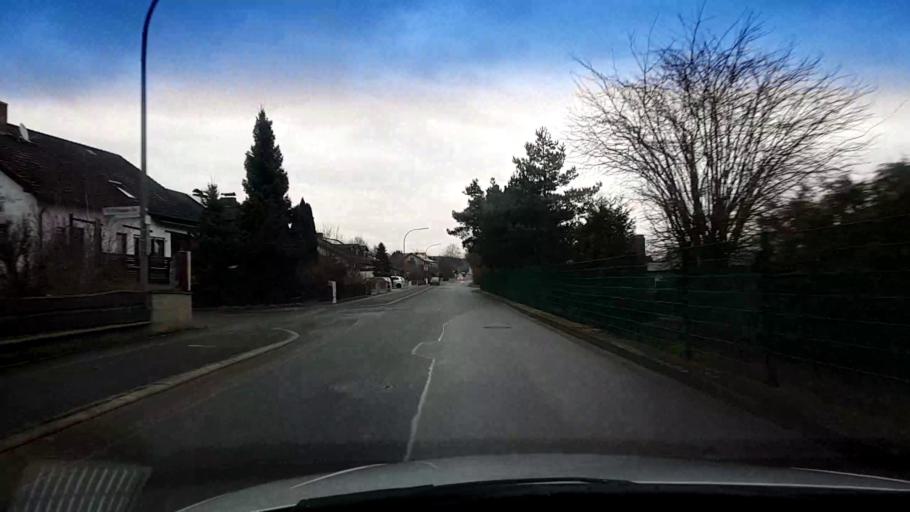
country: DE
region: Bavaria
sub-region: Upper Franconia
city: Oberhaid
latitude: 49.9363
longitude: 10.8074
